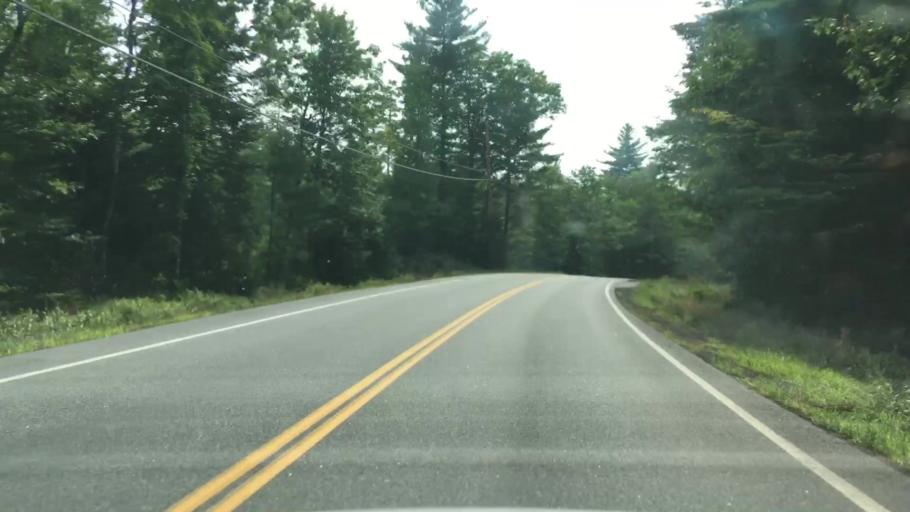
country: US
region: Maine
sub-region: Oxford County
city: Paris
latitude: 44.2398
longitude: -70.4683
